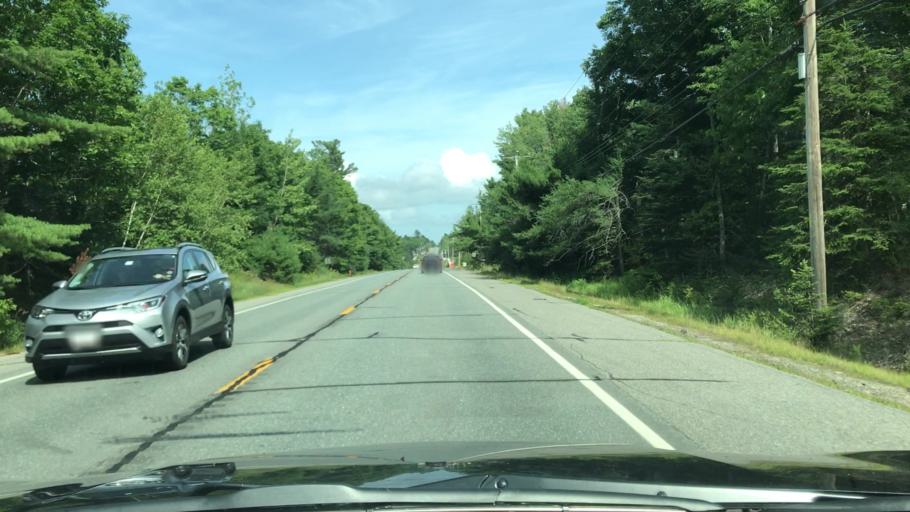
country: US
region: Maine
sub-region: Hancock County
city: Ellsworth
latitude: 44.5395
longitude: -68.4644
